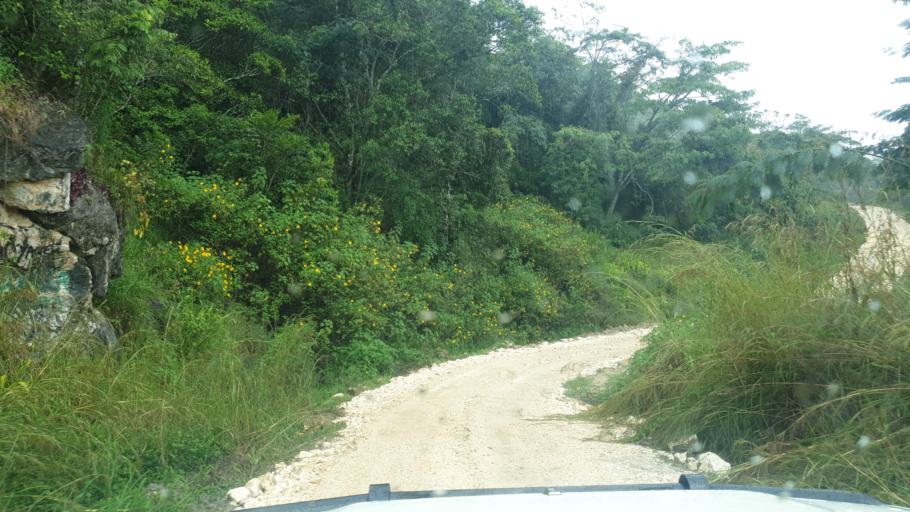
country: PG
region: Eastern Highlands
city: Goroka
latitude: -6.1984
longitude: 145.2141
